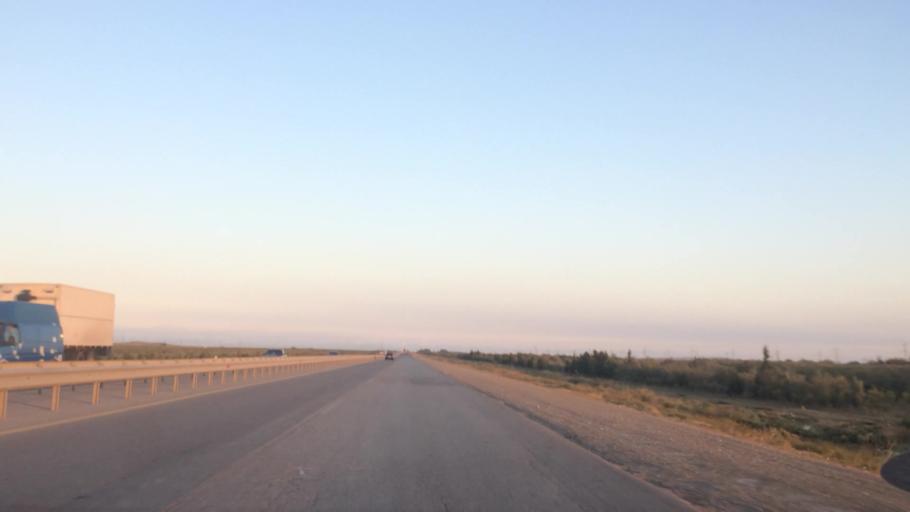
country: AZ
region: Baki
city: Qobustan
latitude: 39.9607
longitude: 49.2931
